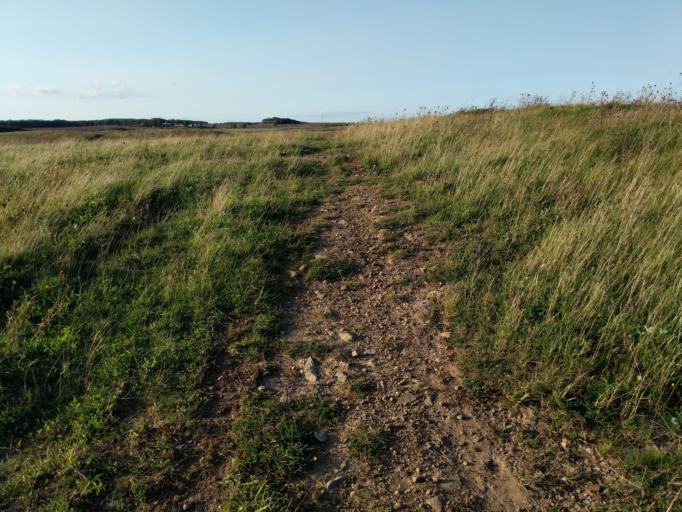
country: GB
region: England
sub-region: Northumberland
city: Lynemouth
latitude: 55.2108
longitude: -1.5256
